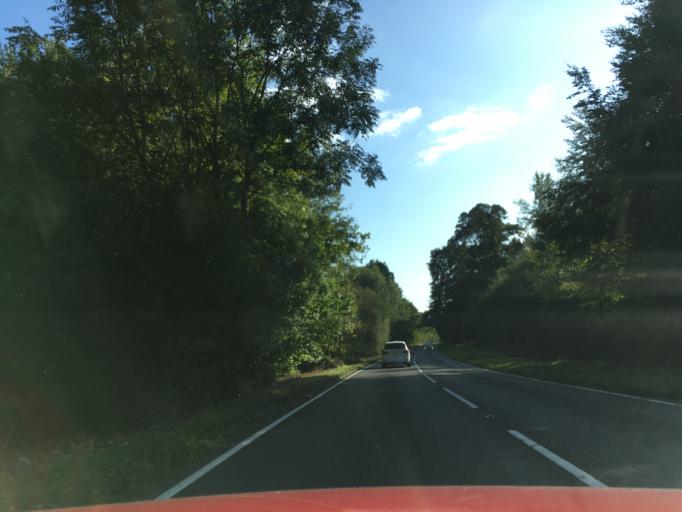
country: GB
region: England
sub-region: Hampshire
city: Alton
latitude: 51.1262
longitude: -0.9922
